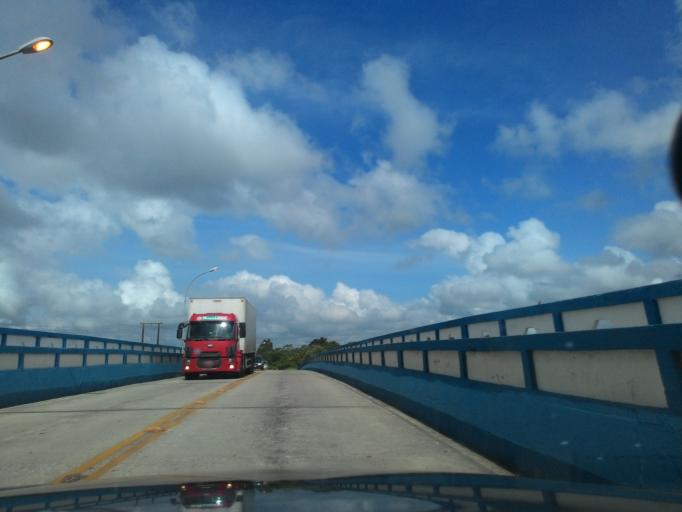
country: BR
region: Sao Paulo
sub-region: Iguape
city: Iguape
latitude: -24.6947
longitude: -47.5681
